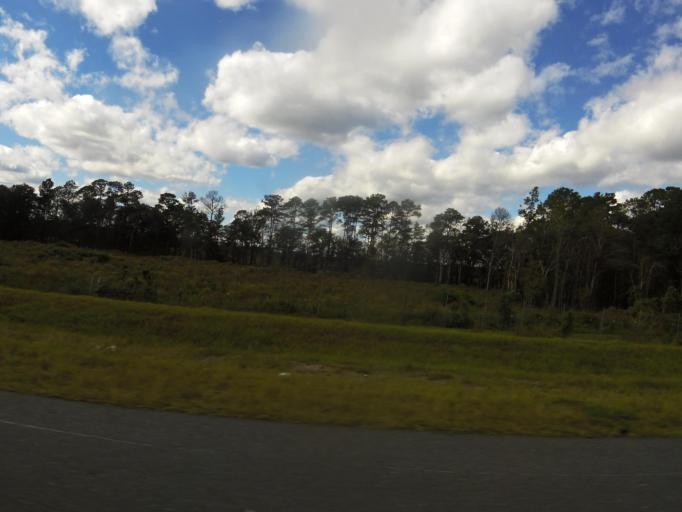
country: US
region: Florida
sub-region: Bradford County
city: Starke
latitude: 29.9570
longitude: -82.1363
